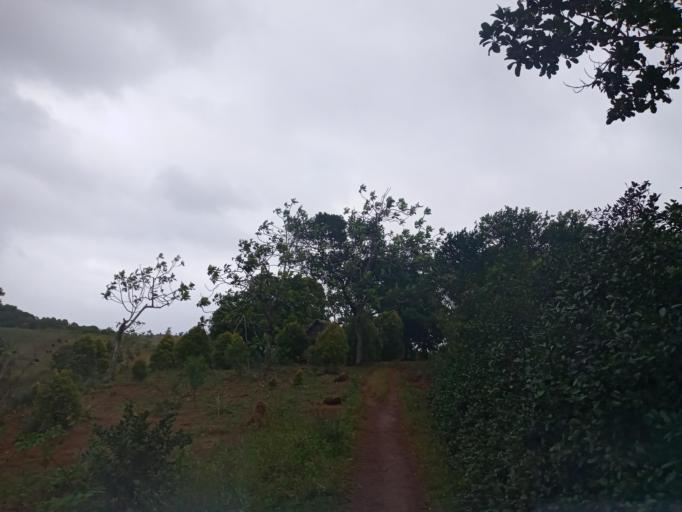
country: MG
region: Atsimo-Atsinanana
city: Vohipaho
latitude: -23.8285
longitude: 47.5429
